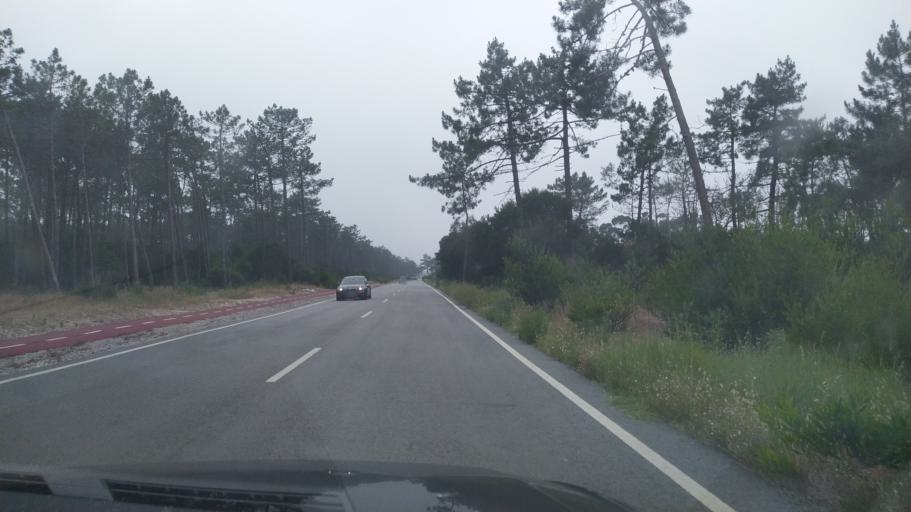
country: PT
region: Aveiro
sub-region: Ilhavo
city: Gafanha da Encarnacao
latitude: 40.5649
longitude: -8.7410
